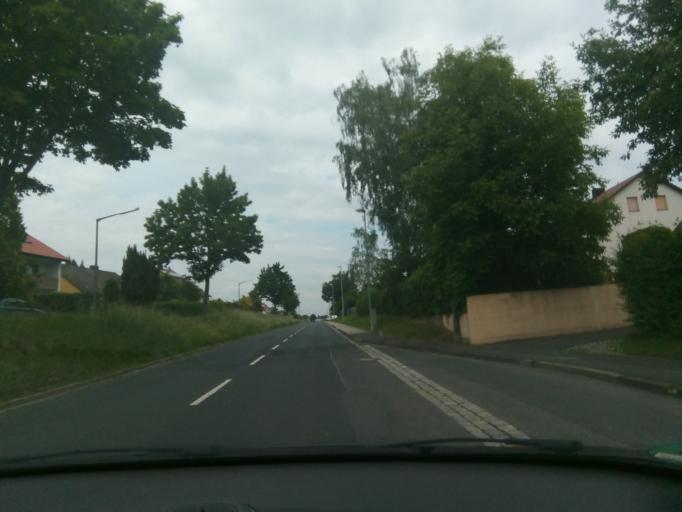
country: DE
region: Bavaria
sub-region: Regierungsbezirk Unterfranken
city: Kurnach
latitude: 49.8482
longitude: 10.0453
